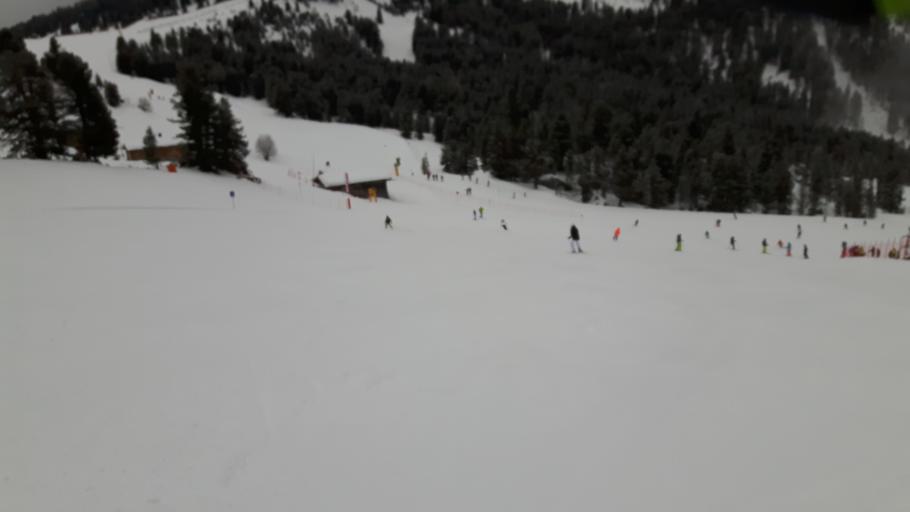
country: IT
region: Trentino-Alto Adige
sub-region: Bolzano
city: Nova Levante
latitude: 46.3592
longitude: 11.5418
